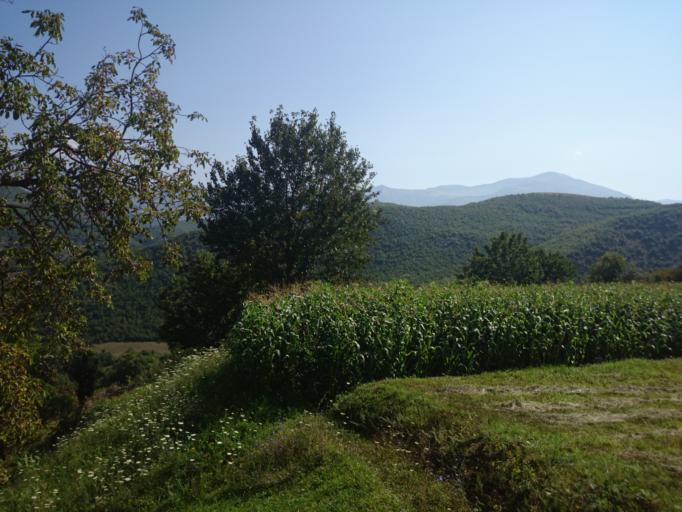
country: AL
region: Diber
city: Peshkopi
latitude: 41.6333
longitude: 20.4082
